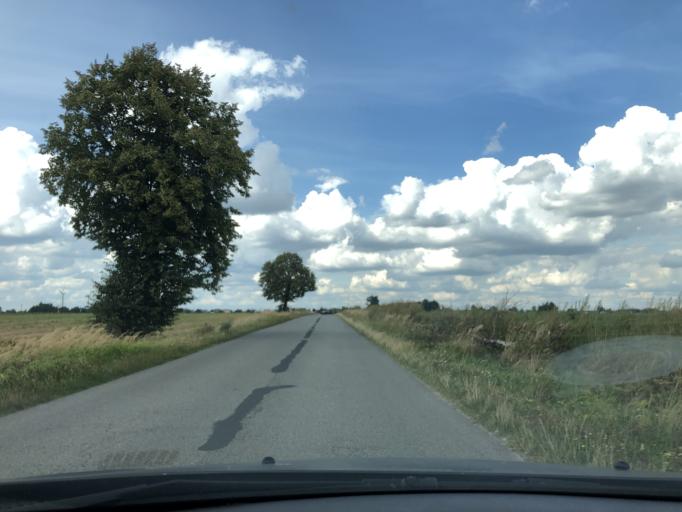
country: PL
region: Lodz Voivodeship
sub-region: Powiat wieruszowski
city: Walichnowy
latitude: 51.2520
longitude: 18.3900
